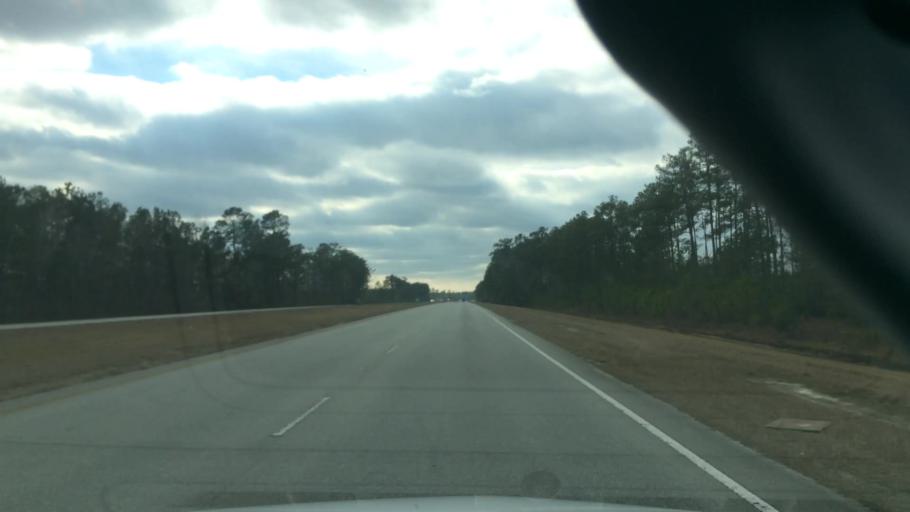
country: US
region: North Carolina
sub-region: Brunswick County
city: Bolivia
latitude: 34.0598
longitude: -78.2054
